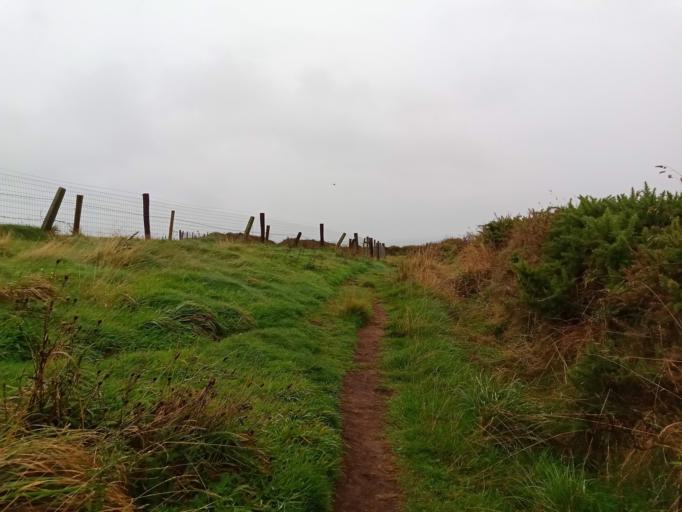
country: IE
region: Munster
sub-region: Waterford
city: Dunmore East
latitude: 52.1392
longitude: -7.0550
